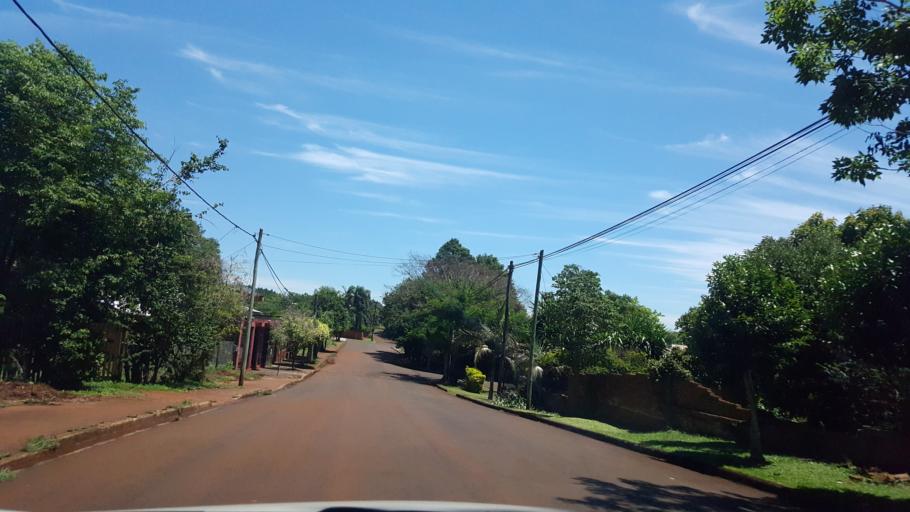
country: AR
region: Misiones
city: Capiovi
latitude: -26.9322
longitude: -55.0562
